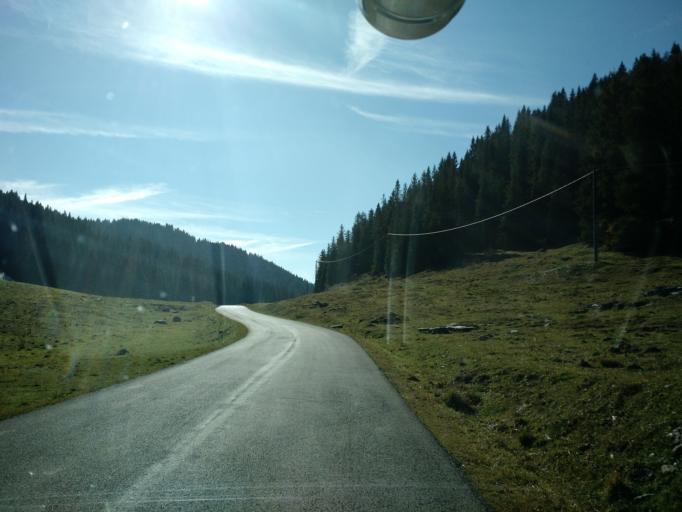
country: IT
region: Veneto
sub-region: Provincia di Vicenza
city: Gallio
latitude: 45.9321
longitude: 11.5585
